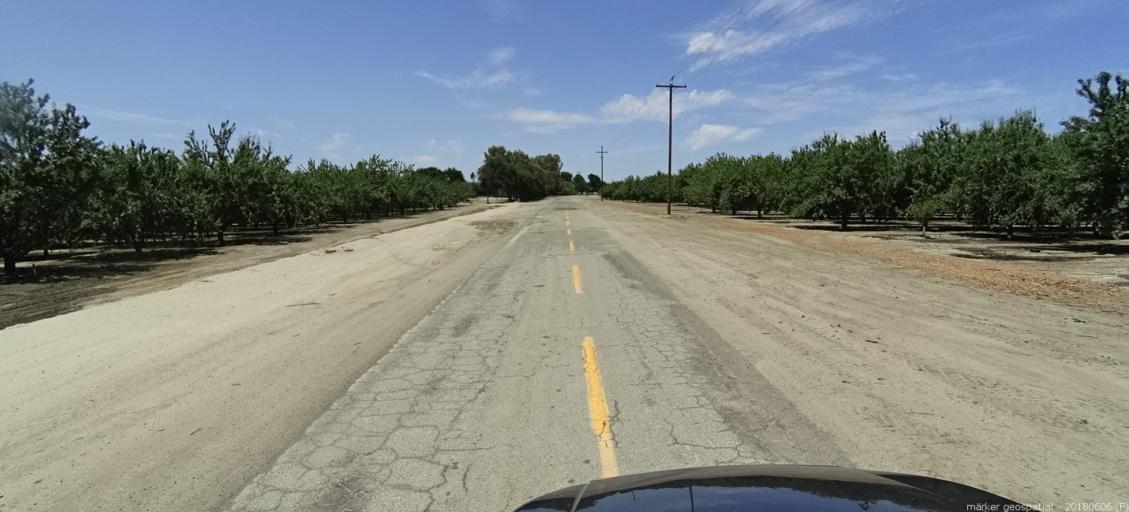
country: US
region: California
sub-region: Fresno County
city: Mendota
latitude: 36.8062
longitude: -120.3485
